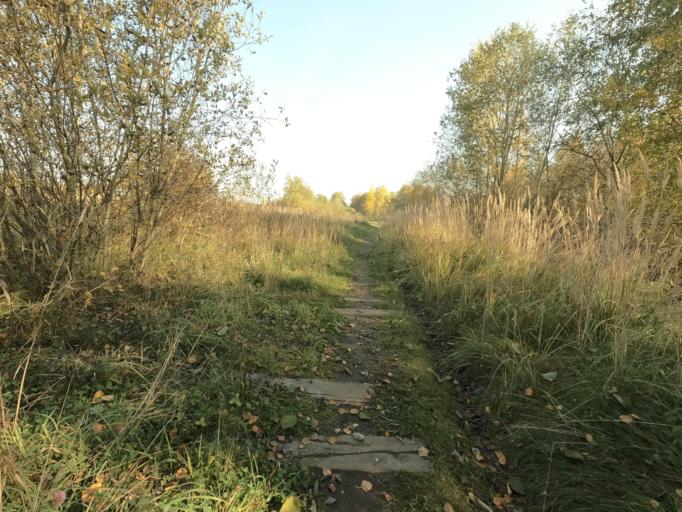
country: RU
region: Leningrad
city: Mga
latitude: 59.7484
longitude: 31.0700
